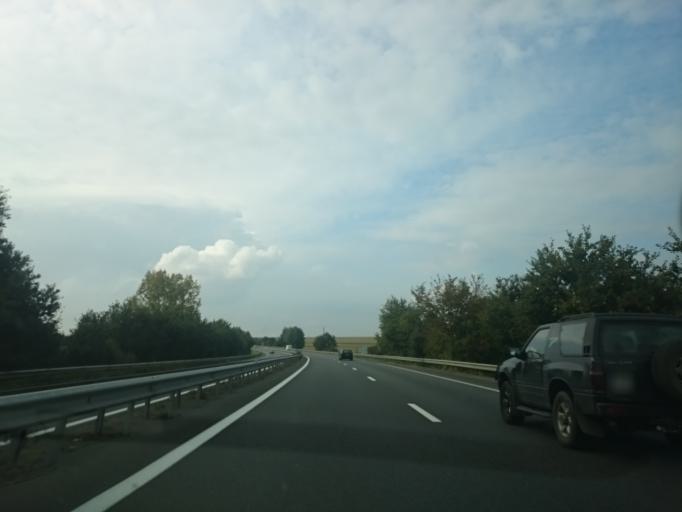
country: FR
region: Brittany
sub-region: Departement des Cotes-d'Armor
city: Broons
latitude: 48.3354
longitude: -2.2693
